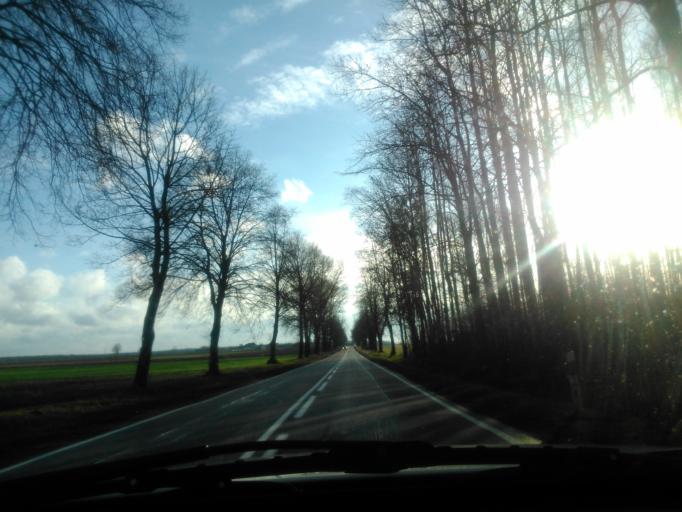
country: PL
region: Podlasie
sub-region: Powiat kolnenski
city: Maly Plock
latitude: 53.3360
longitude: 22.0080
